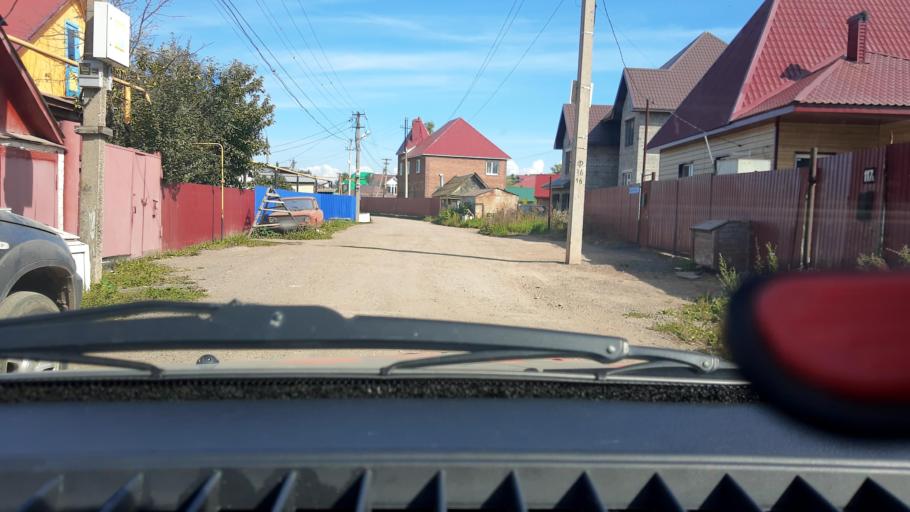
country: RU
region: Bashkortostan
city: Ufa
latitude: 54.6932
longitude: 55.9525
